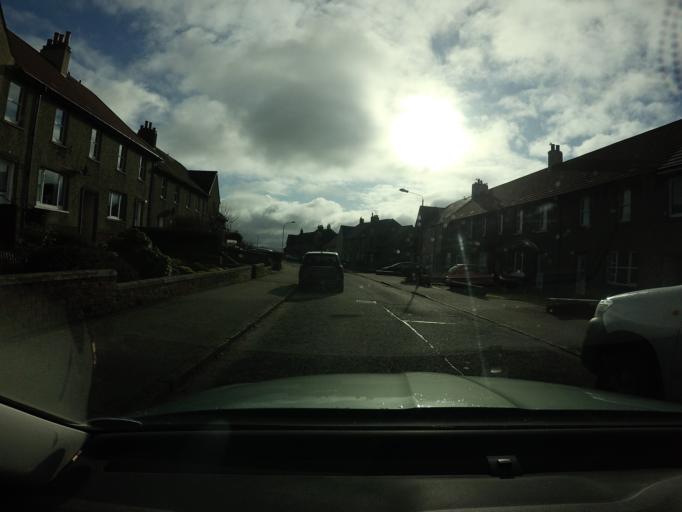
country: GB
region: Scotland
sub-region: South Lanarkshire
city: Forth
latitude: 55.7633
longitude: -3.6946
